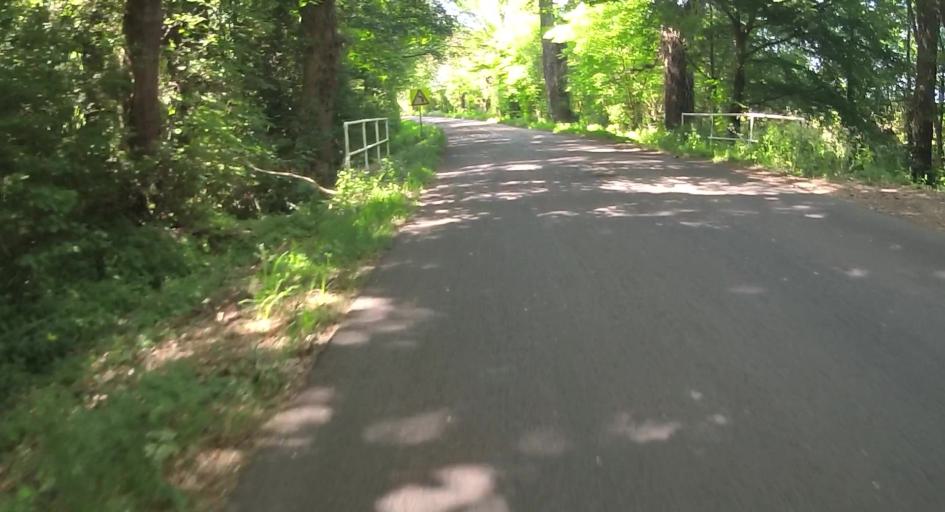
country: GB
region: England
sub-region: Wokingham
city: Swallowfield
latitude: 51.3609
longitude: -0.9877
